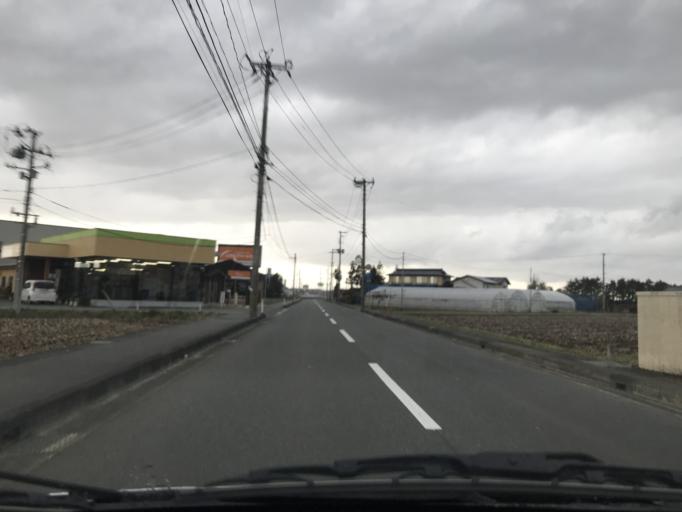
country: JP
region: Iwate
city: Mizusawa
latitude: 39.1630
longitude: 141.1480
